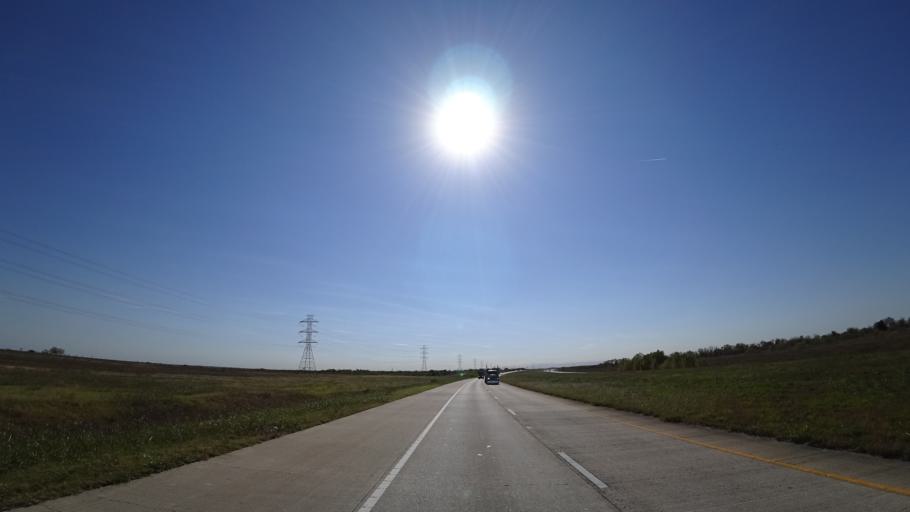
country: US
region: Texas
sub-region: Travis County
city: Manor
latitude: 30.3892
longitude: -97.5783
